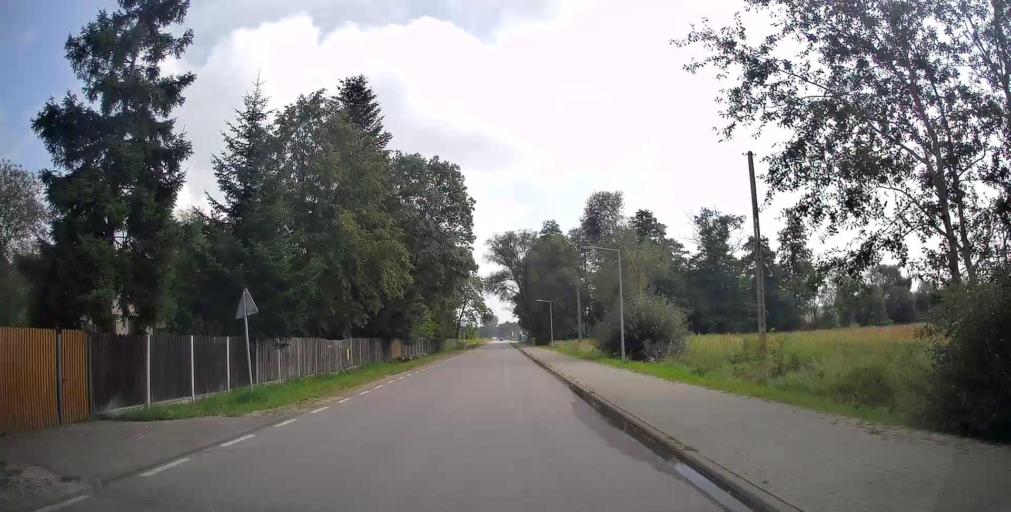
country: PL
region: Masovian Voivodeship
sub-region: Powiat bialobrzeski
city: Sucha
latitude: 51.6178
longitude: 20.9555
